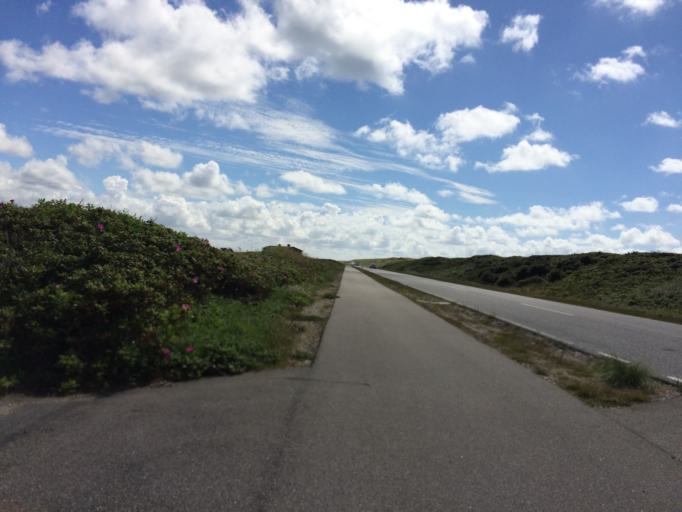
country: DK
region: Central Jutland
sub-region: Holstebro Kommune
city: Ulfborg
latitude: 56.3648
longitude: 8.1228
